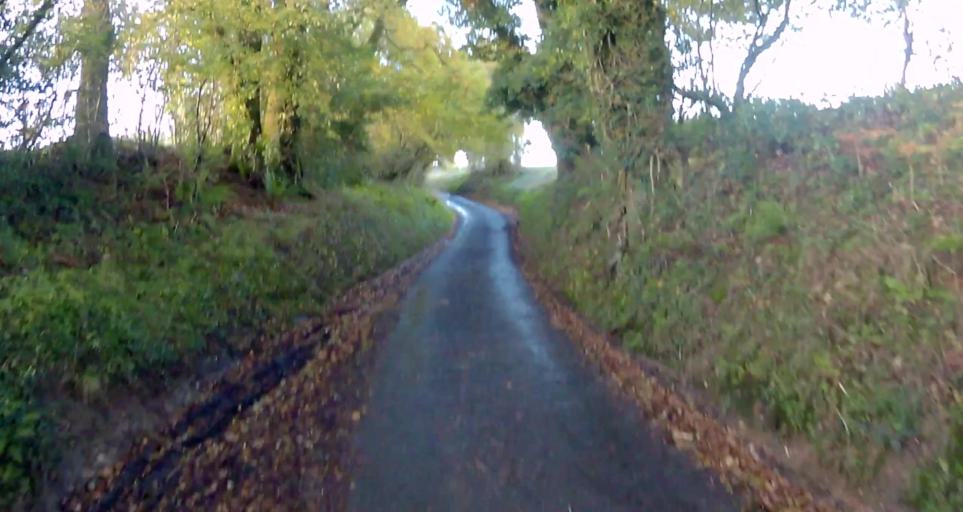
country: GB
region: England
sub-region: Hampshire
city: Basingstoke
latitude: 51.2103
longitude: -1.0886
